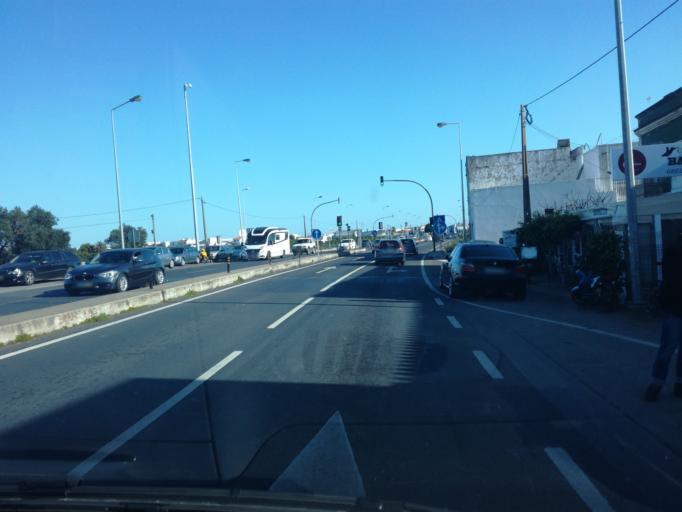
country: PT
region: Faro
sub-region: Olhao
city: Olhao
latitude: 37.0306
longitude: -7.8647
